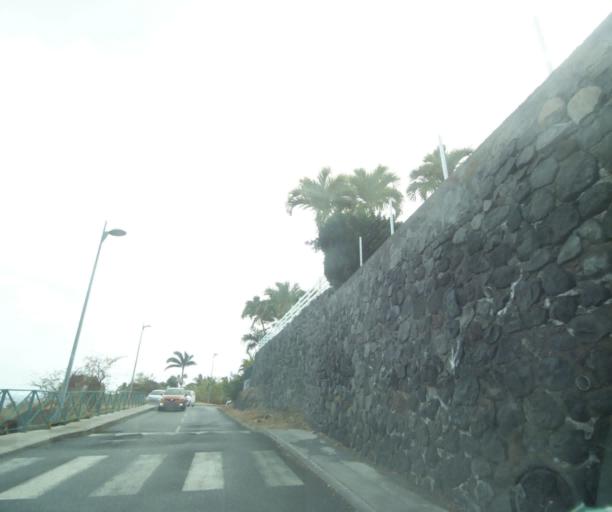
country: RE
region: Reunion
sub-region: Reunion
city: Saint-Paul
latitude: -21.0464
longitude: 55.2253
